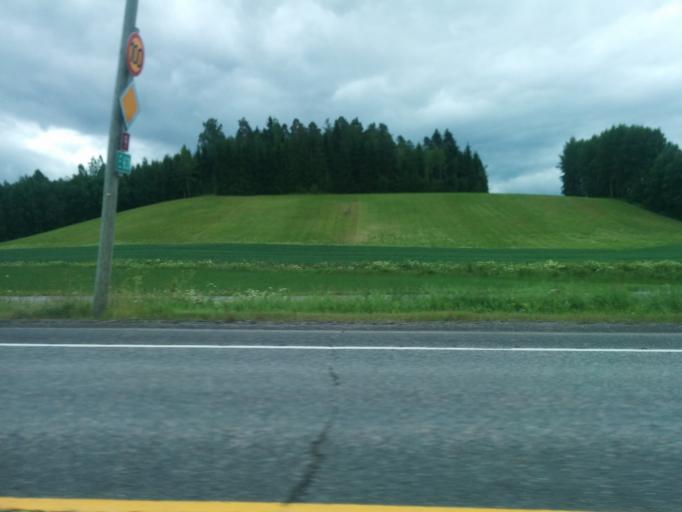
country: FI
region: Pirkanmaa
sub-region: Tampere
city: Orivesi
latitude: 61.6921
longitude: 24.4083
